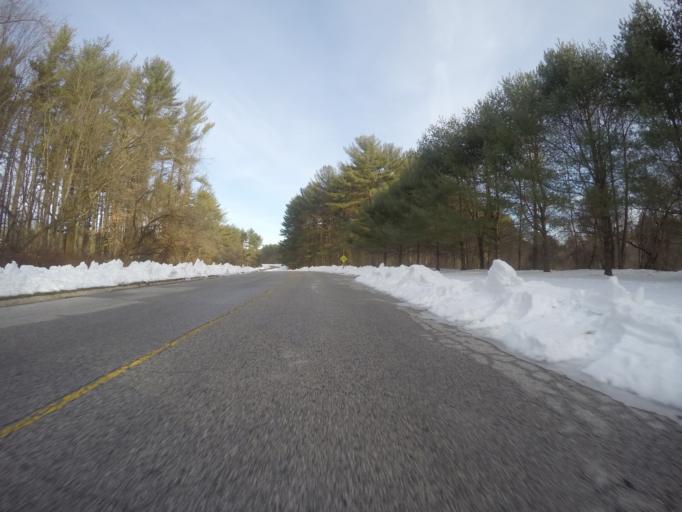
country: US
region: Maryland
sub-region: Baltimore County
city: Hampton
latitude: 39.4453
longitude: -76.5922
